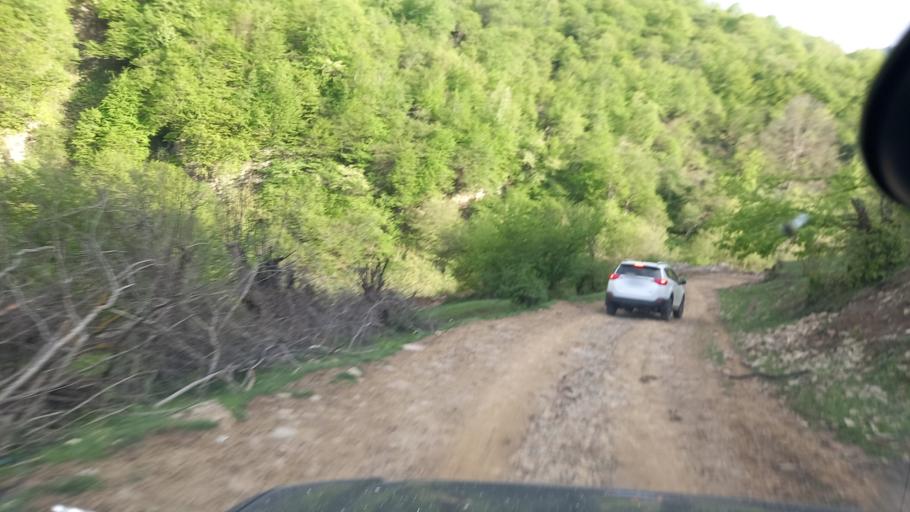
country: RU
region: Dagestan
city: Khuchni
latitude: 41.9453
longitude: 47.8350
